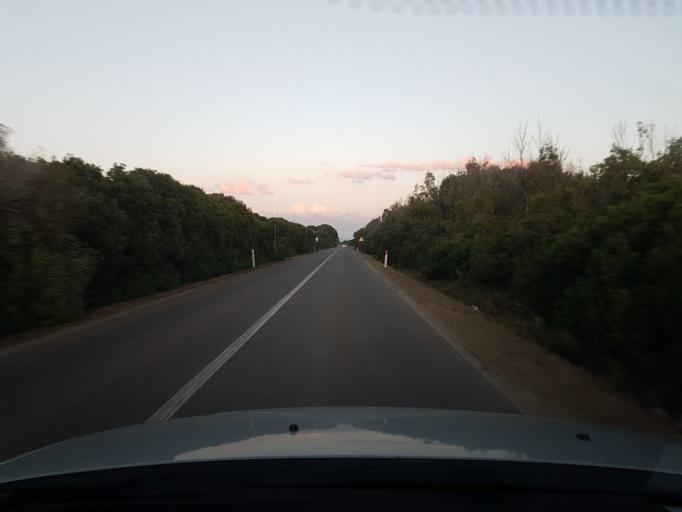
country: IT
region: Sardinia
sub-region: Provincia di Oristano
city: Riola Sardo
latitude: 40.0245
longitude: 8.4419
